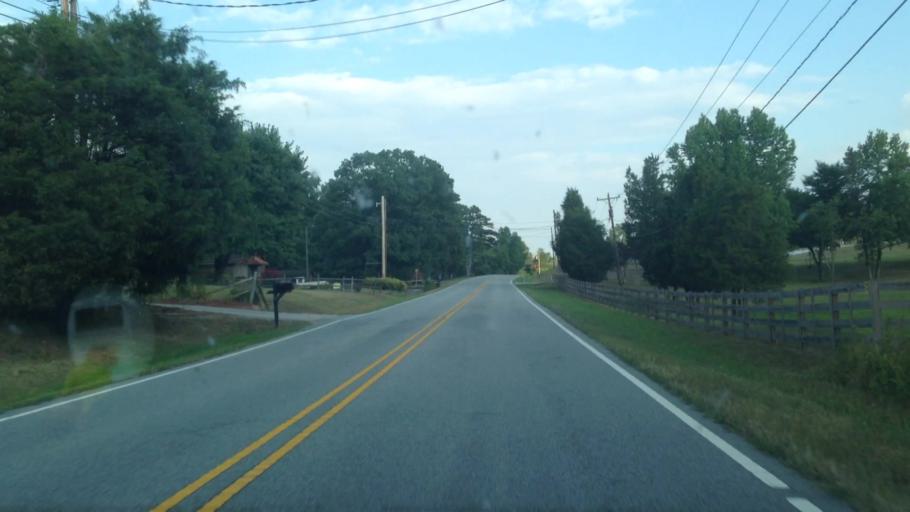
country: US
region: North Carolina
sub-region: Guilford County
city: High Point
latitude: 35.9609
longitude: -80.0753
